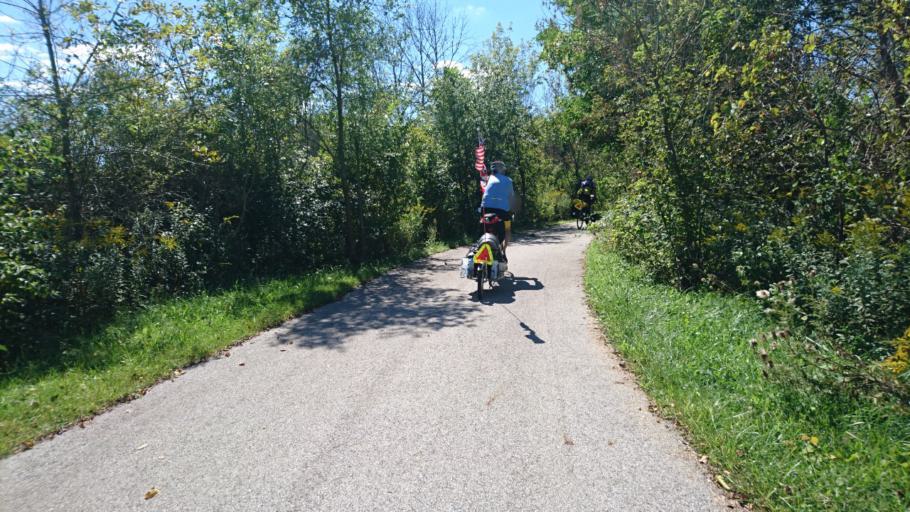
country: US
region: Illinois
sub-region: Cook County
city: Glenwood
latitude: 41.5444
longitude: -87.5719
